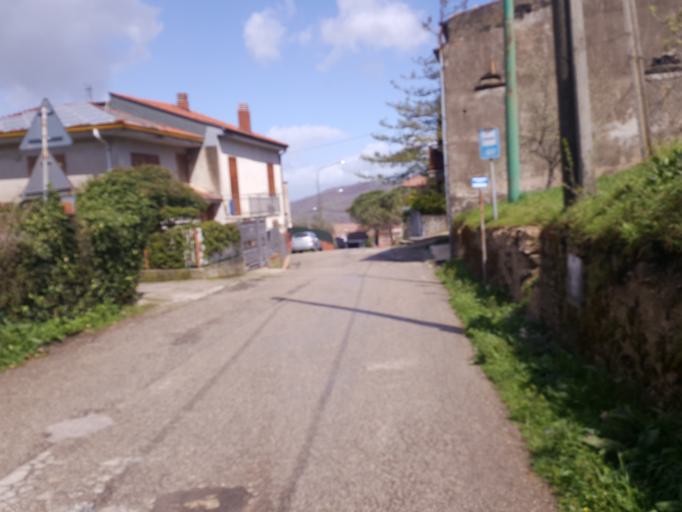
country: IT
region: Campania
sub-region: Provincia di Avellino
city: Roccabascerana
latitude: 41.0420
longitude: 14.7177
